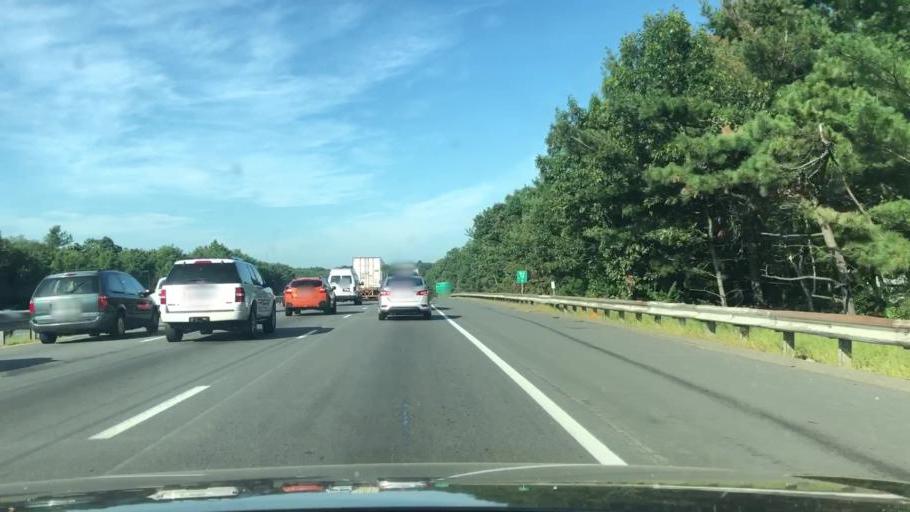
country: US
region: Massachusetts
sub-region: Essex County
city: Lawrence
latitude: 42.6762
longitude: -71.1670
